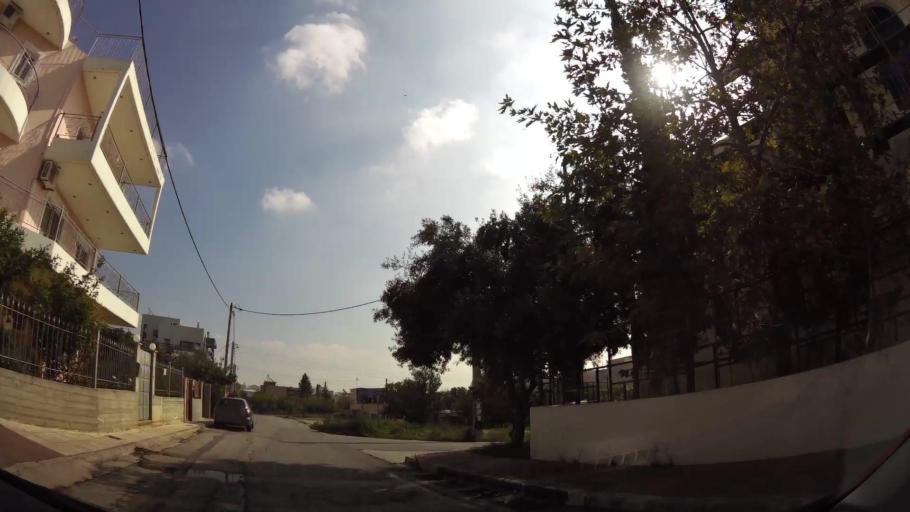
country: GR
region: Attica
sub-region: Nomarchia Dytikis Attikis
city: Zefyri
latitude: 38.0555
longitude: 23.7269
